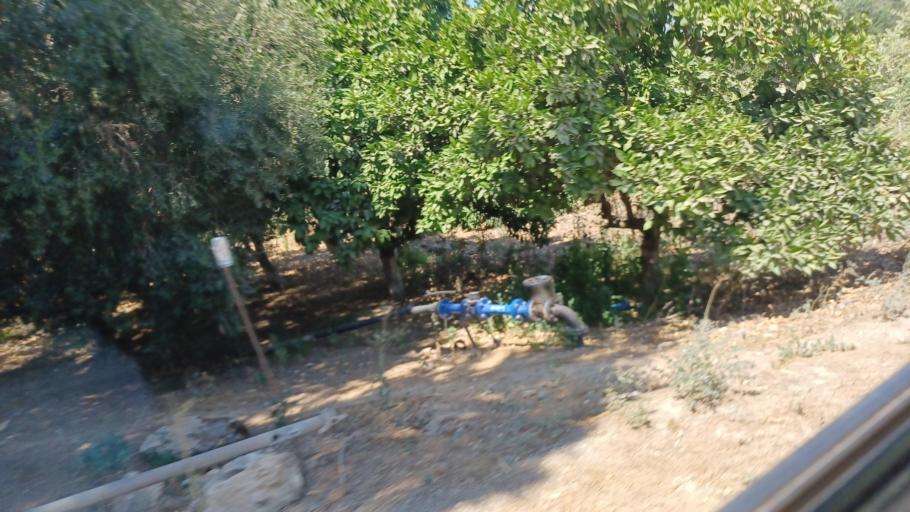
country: CY
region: Ammochostos
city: Acheritou
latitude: 35.0836
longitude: 33.8878
